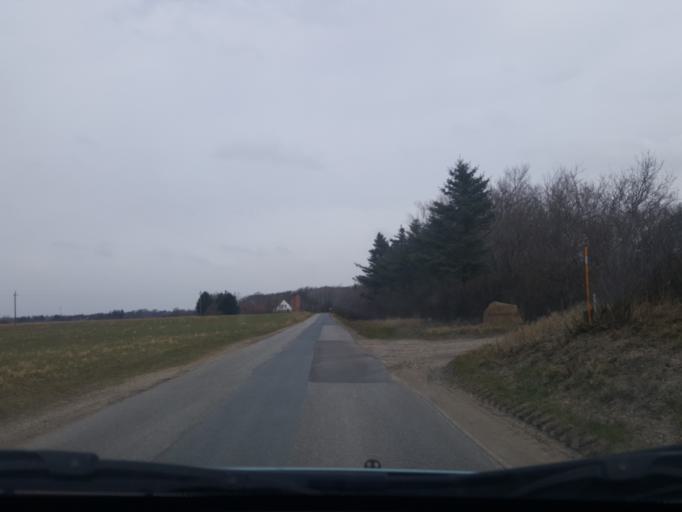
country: DK
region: Central Jutland
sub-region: Holstebro Kommune
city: Ulfborg
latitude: 56.2202
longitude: 8.2633
